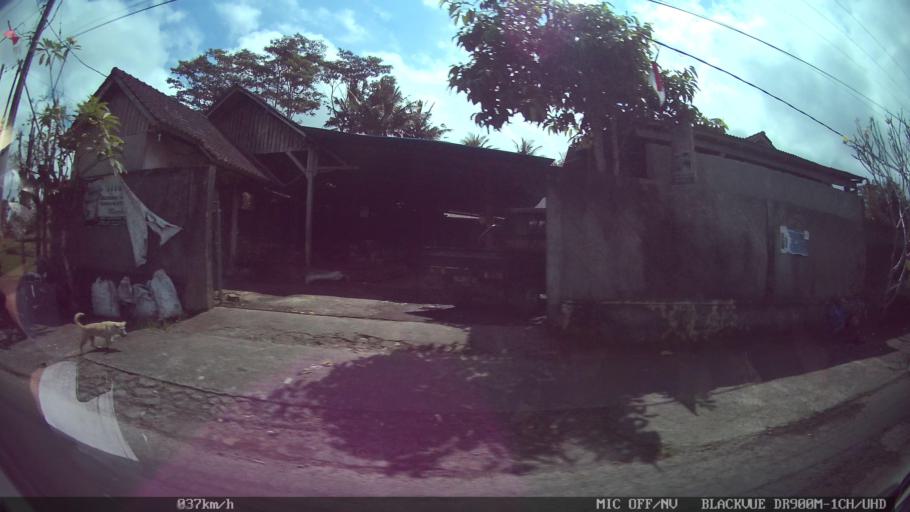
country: ID
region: Bali
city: Banjar Abuan
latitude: -8.4604
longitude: 115.3233
